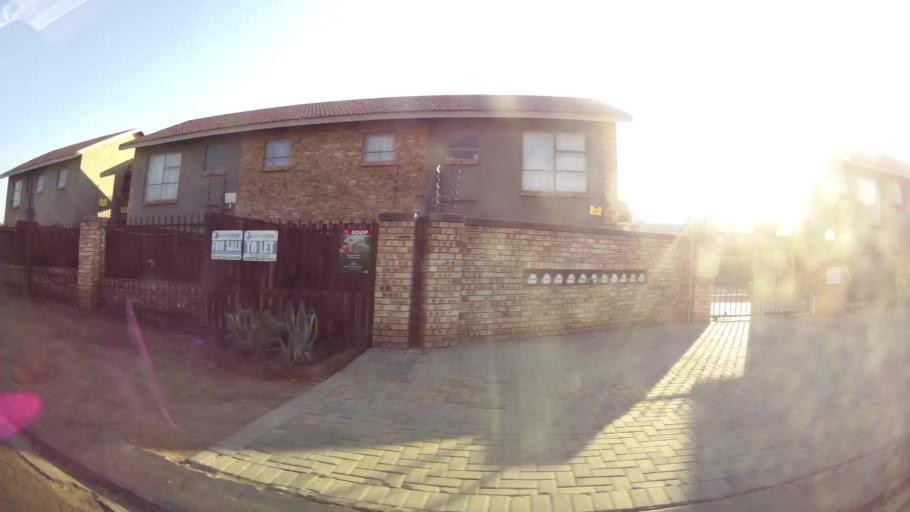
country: ZA
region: Orange Free State
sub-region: Mangaung Metropolitan Municipality
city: Bloemfontein
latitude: -29.1661
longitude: 26.1772
